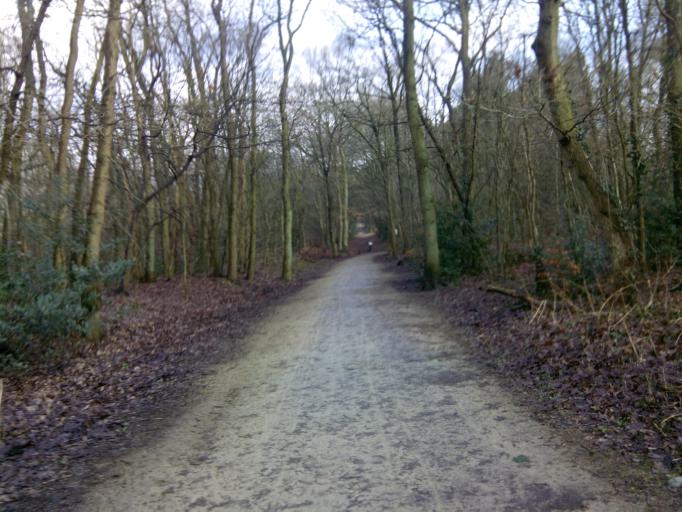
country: NL
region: Utrecht
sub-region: Gemeente Utrechtse Heuvelrug
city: Amerongen
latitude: 52.0023
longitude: 5.4694
